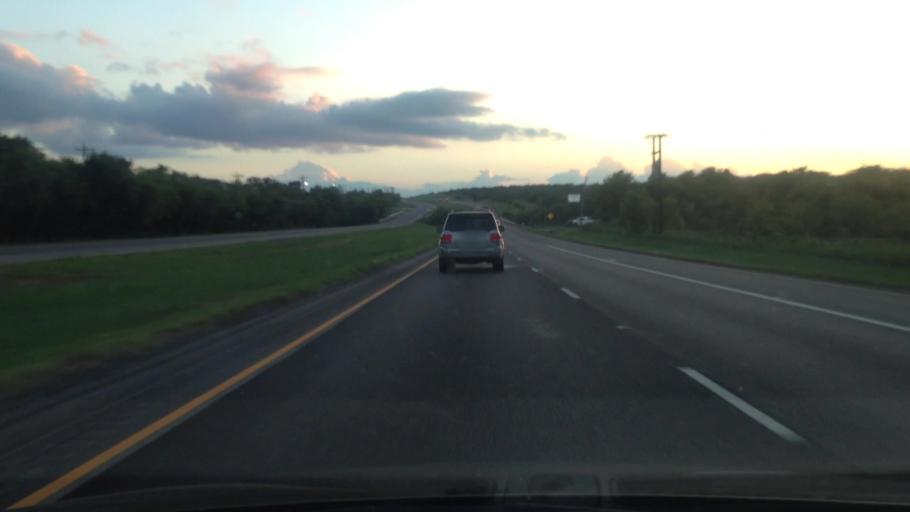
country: US
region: Texas
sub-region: Parker County
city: Aledo
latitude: 32.5988
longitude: -97.5725
